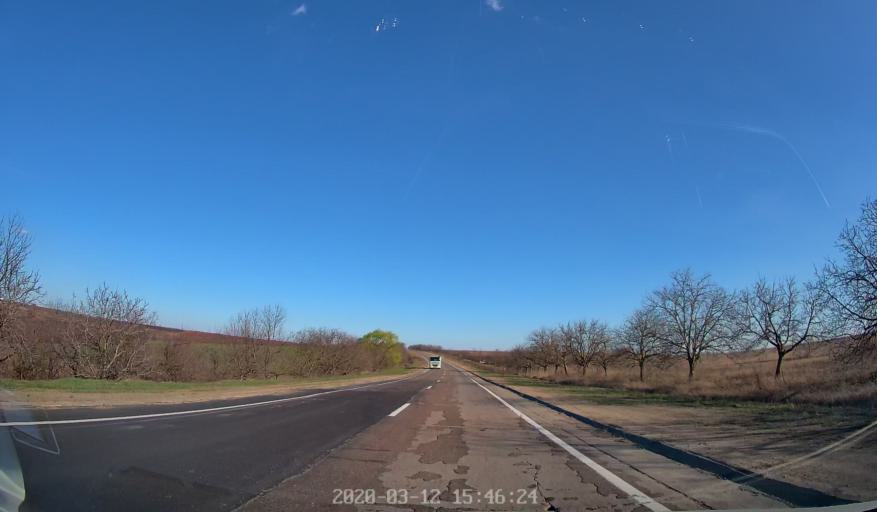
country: MD
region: Chisinau
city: Stauceni
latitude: 47.0997
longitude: 28.8920
